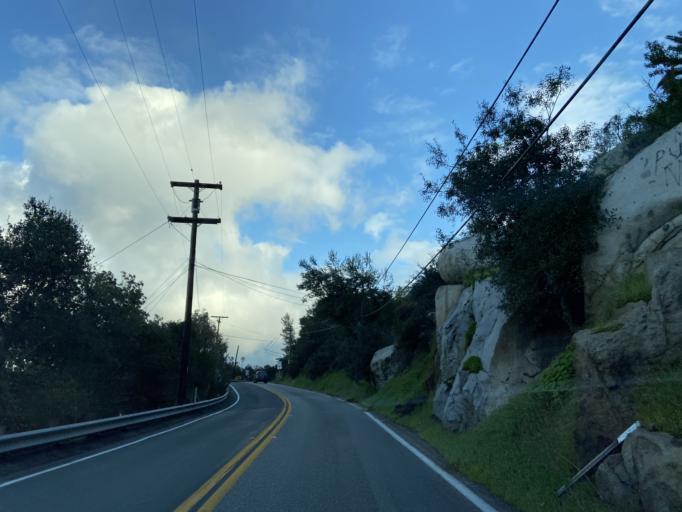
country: US
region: California
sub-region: San Diego County
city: Casa de Oro-Mount Helix
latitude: 32.7764
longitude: -116.9901
